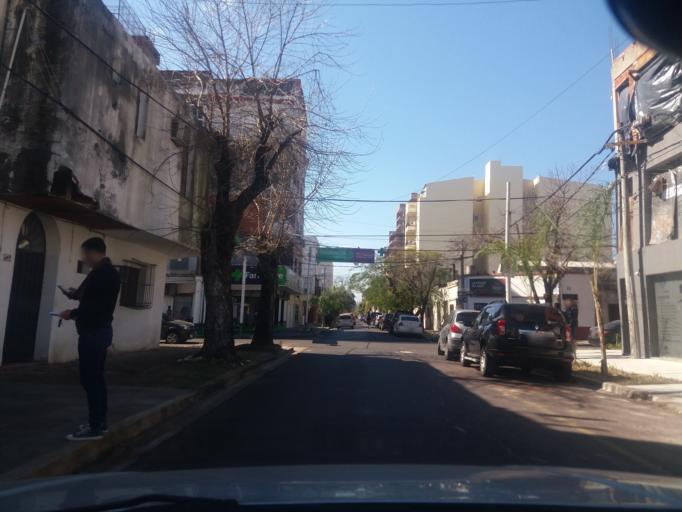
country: AR
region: Corrientes
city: Corrientes
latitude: -27.4726
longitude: -58.8449
